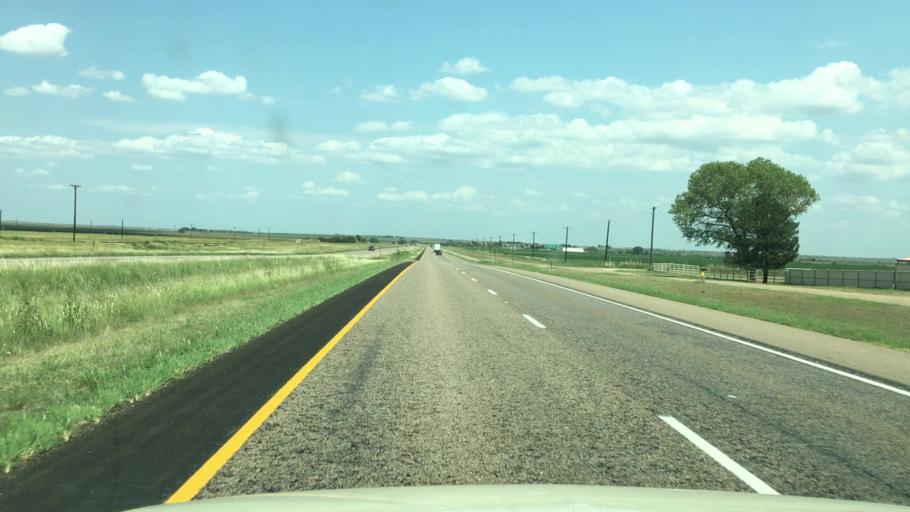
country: US
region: Texas
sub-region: Donley County
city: Clarendon
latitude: 35.0315
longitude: -101.1172
